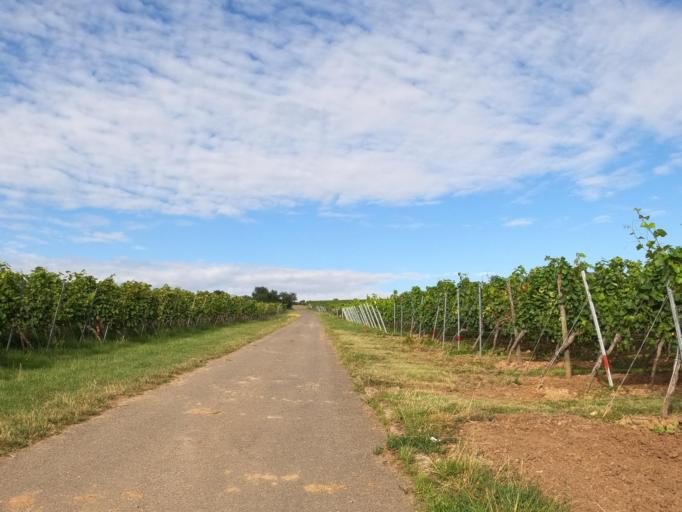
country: DE
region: Rheinland-Pfalz
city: Dackenheim
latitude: 49.5159
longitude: 8.1863
